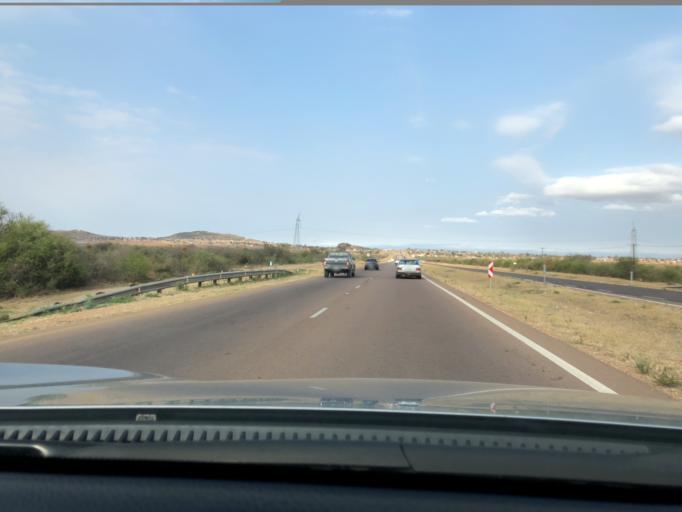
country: ZA
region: Limpopo
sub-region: Capricorn District Municipality
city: Polokwane
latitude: -23.8951
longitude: 29.6342
